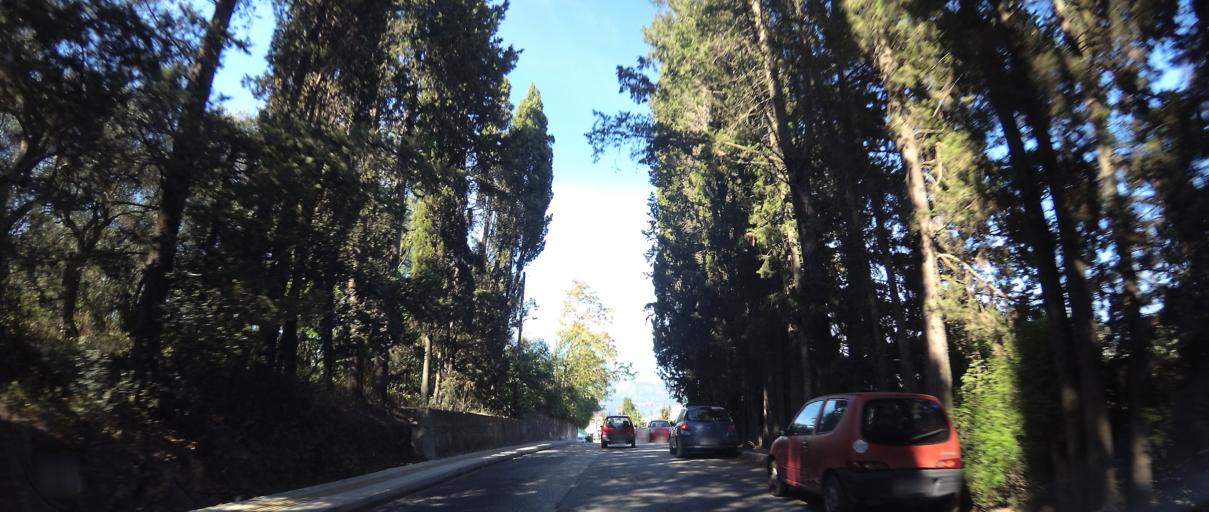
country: GR
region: Ionian Islands
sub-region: Nomos Kerkyras
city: Kontokali
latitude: 39.6511
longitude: 19.8422
